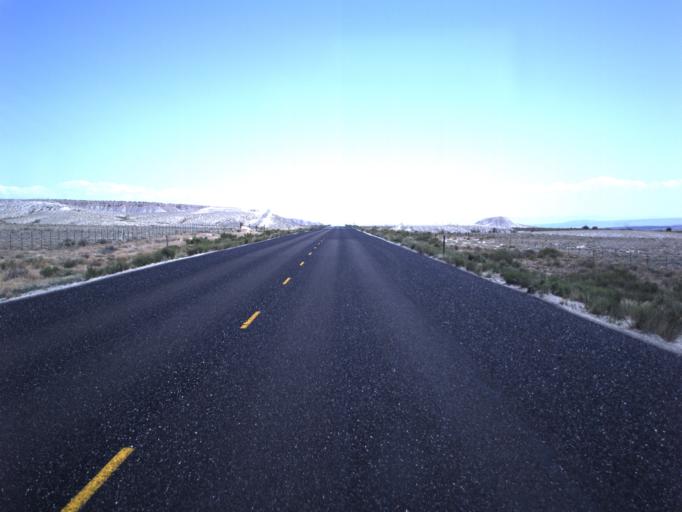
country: US
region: Utah
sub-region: Emery County
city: Ferron
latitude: 38.9976
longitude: -111.1633
